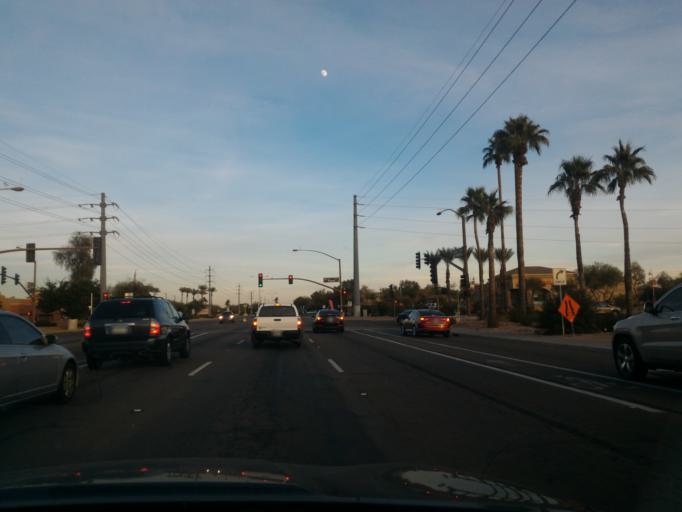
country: US
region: Arizona
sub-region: Maricopa County
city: Guadalupe
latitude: 33.3053
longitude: -111.9464
